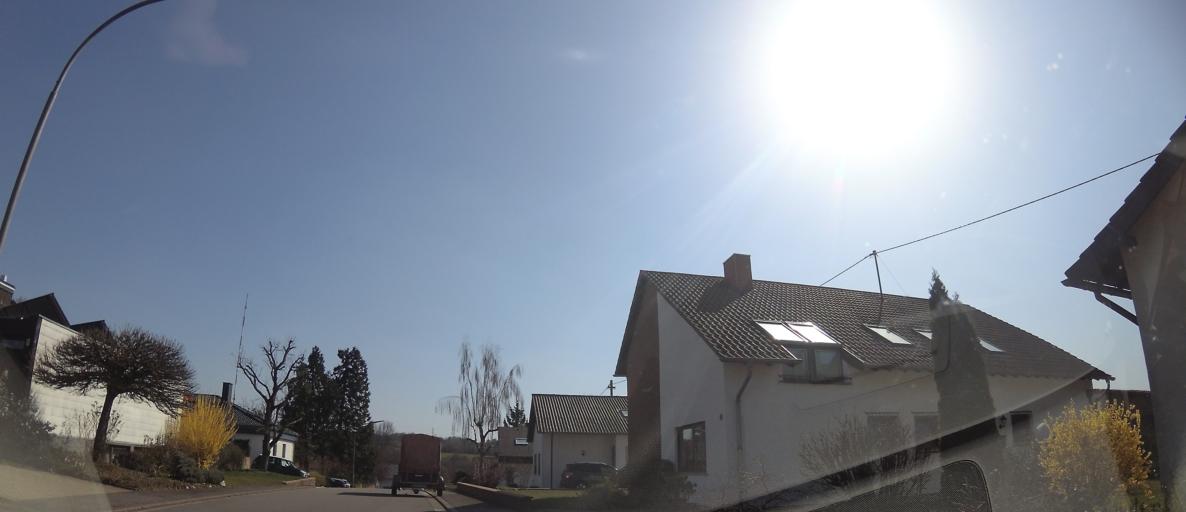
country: DE
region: Saarland
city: Merchweiler
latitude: 49.3470
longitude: 7.0081
